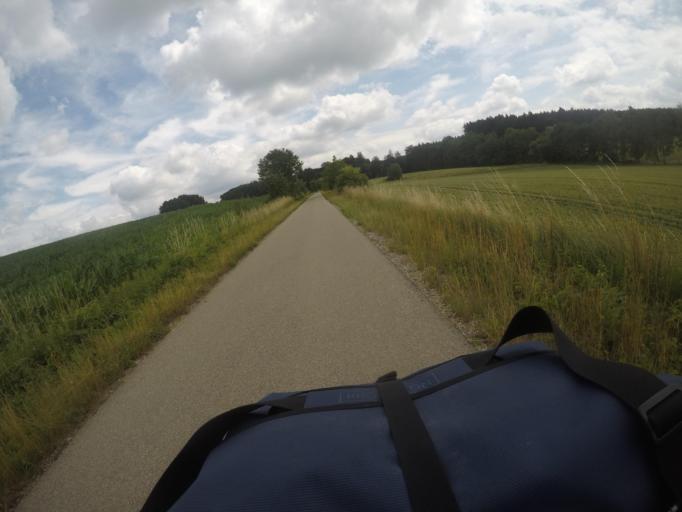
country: DE
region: Bavaria
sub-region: Swabia
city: Kellmunz
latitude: 48.1169
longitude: 10.1466
